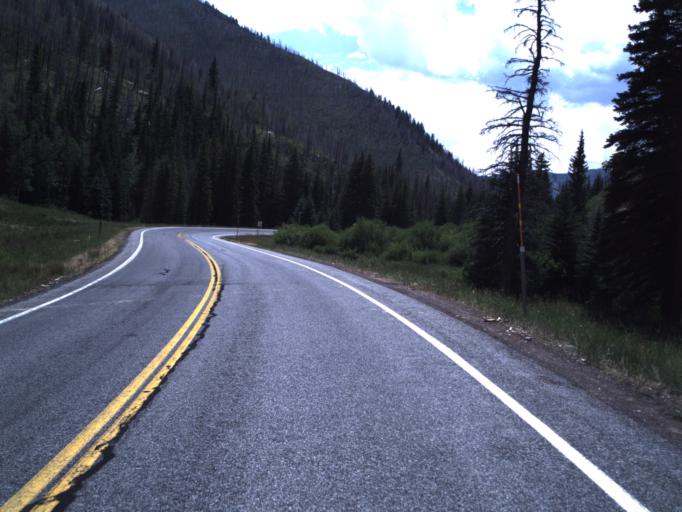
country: US
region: Utah
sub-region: Emery County
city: Huntington
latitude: 39.5263
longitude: -111.1541
